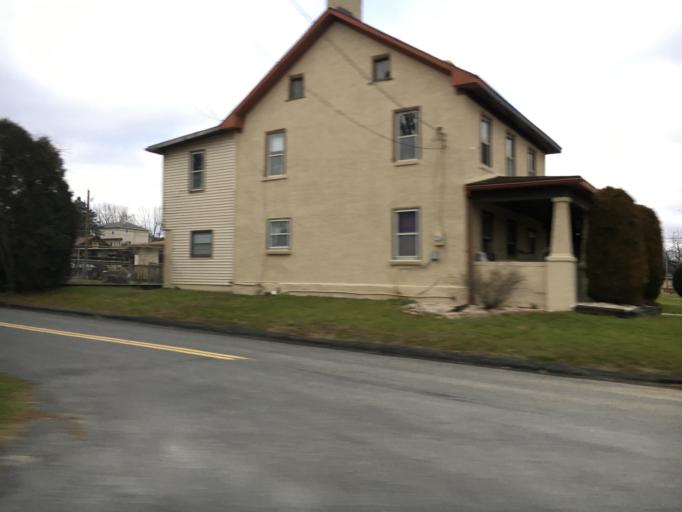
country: US
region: Pennsylvania
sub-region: Lehigh County
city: Egypt
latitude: 40.6787
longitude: -75.5502
